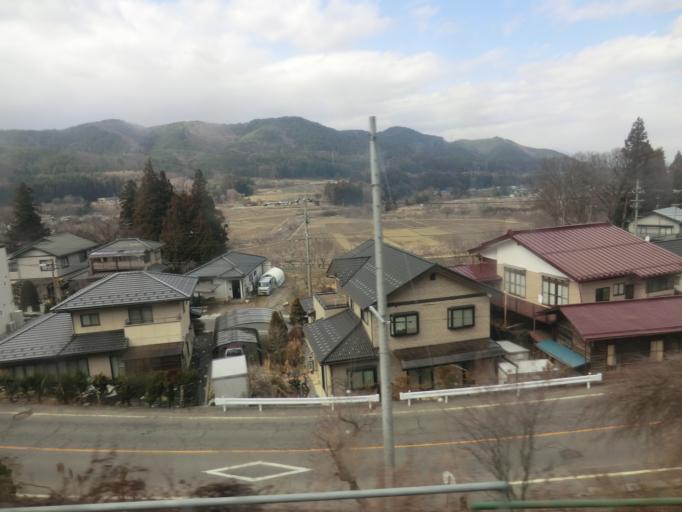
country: JP
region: Nagano
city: Shiojiri
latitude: 36.0901
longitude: 137.9194
